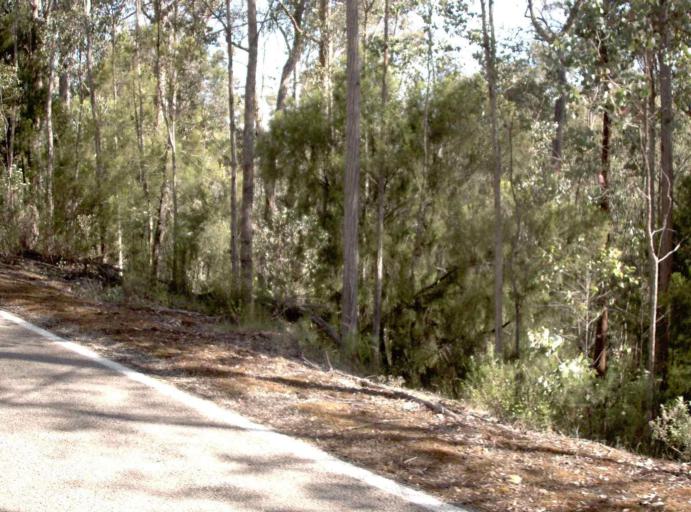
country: AU
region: Victoria
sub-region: East Gippsland
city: Lakes Entrance
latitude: -37.5427
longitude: 148.5465
